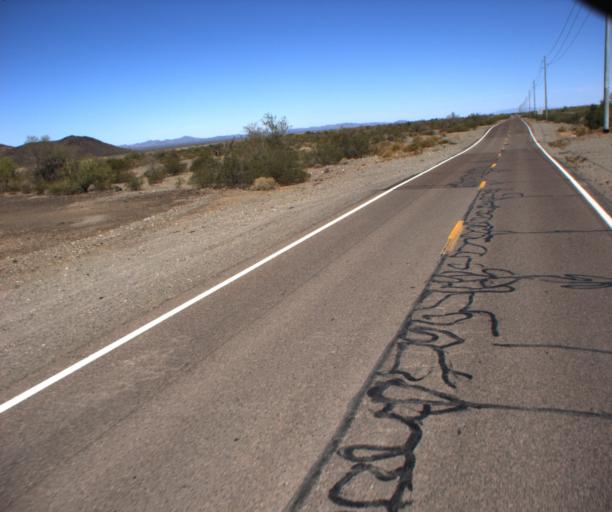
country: US
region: Arizona
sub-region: La Paz County
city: Salome
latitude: 33.7552
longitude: -113.7757
